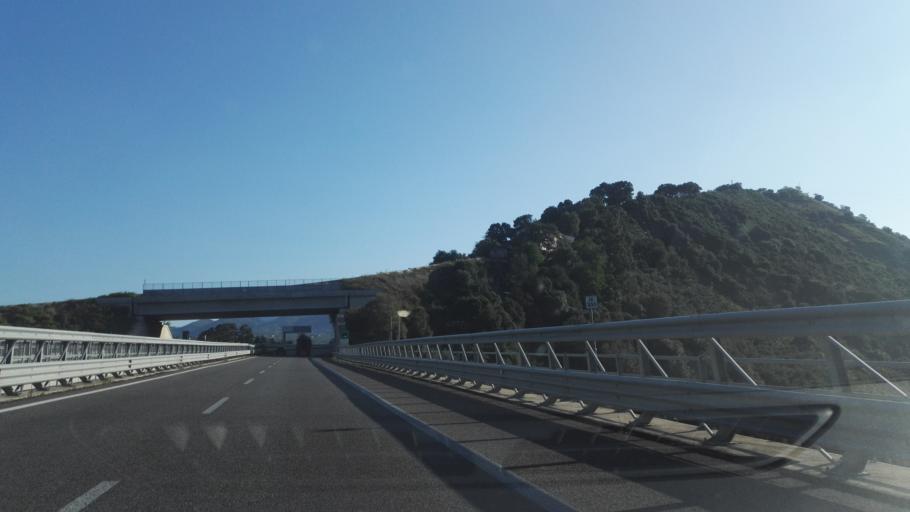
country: IT
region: Calabria
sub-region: Provincia di Catanzaro
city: Nocera Scalo
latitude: 39.0359
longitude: 16.1359
